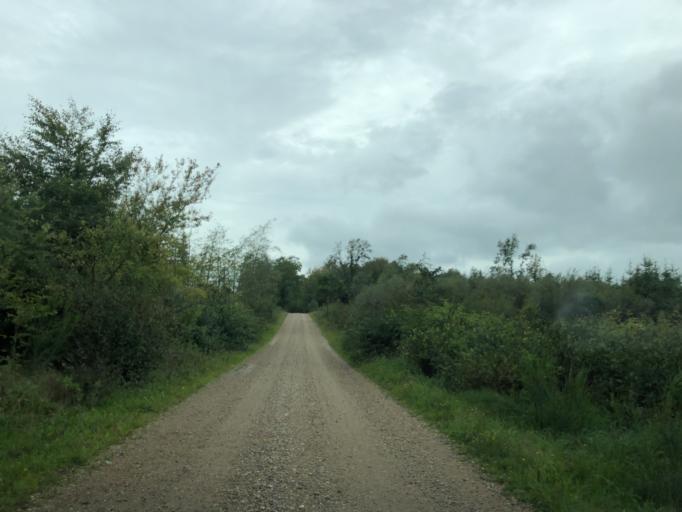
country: DK
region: Central Jutland
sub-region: Holstebro Kommune
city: Holstebro
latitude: 56.2393
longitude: 8.5139
